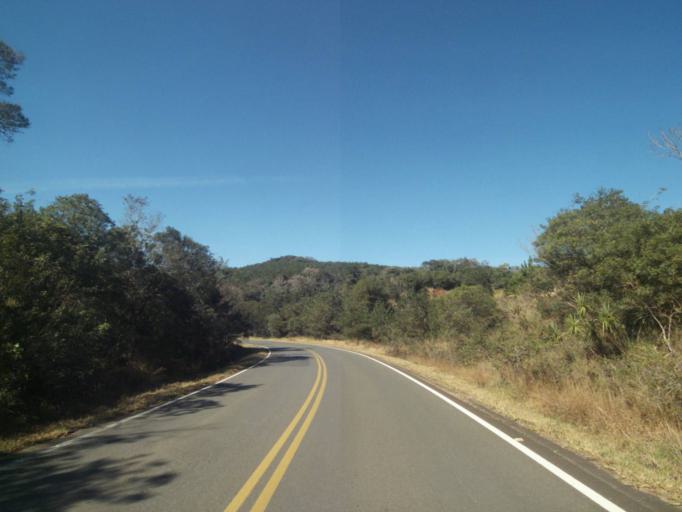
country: BR
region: Parana
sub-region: Telemaco Borba
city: Telemaco Borba
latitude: -24.4232
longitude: -50.5834
